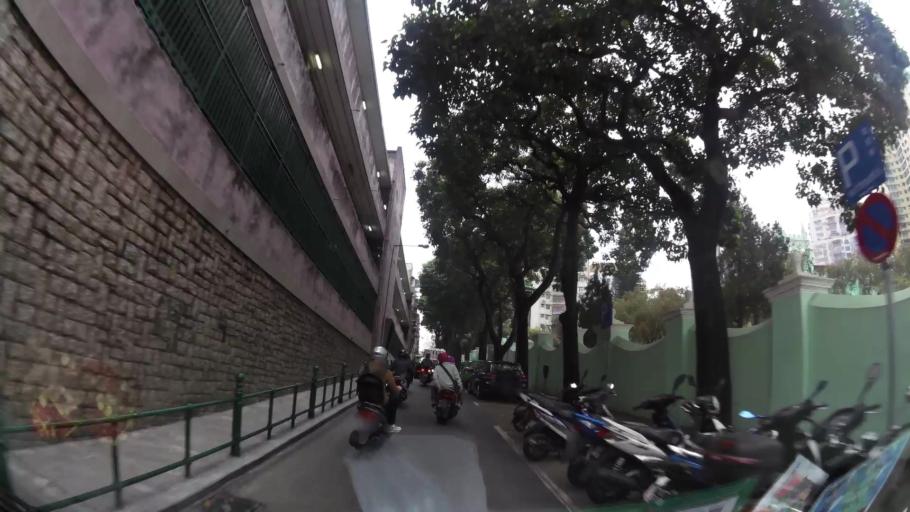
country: MO
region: Macau
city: Macau
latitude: 22.1981
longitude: 113.5459
